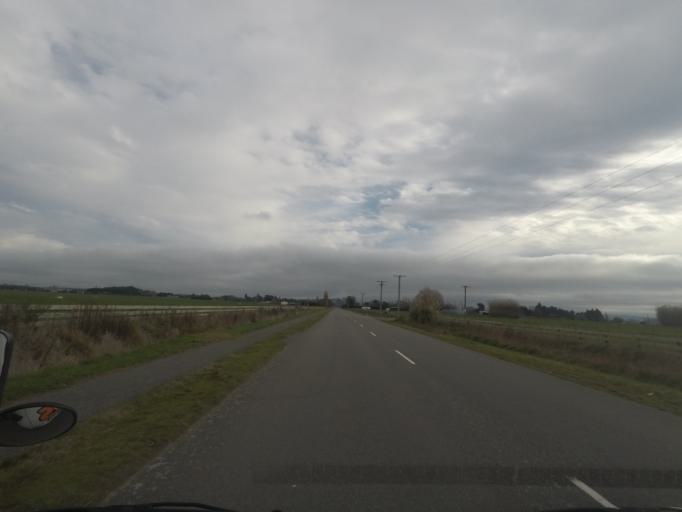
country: NZ
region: Canterbury
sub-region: Waimakariri District
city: Woodend
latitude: -43.2903
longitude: 172.6961
